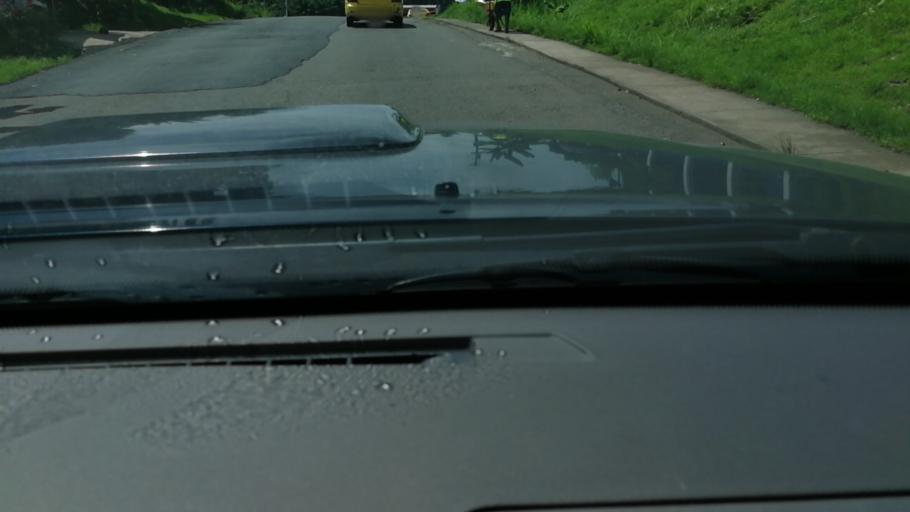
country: PA
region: Panama
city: Tocumen
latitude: 9.0949
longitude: -79.4079
